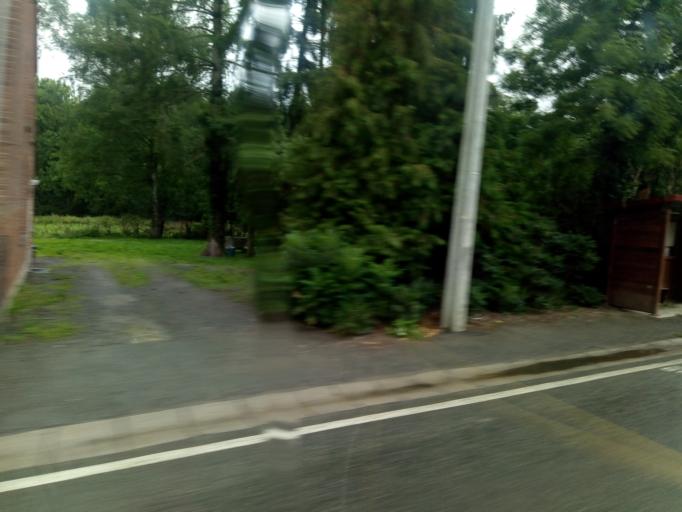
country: BE
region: Wallonia
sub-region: Province du Luxembourg
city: Hotton
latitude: 50.2597
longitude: 5.4667
